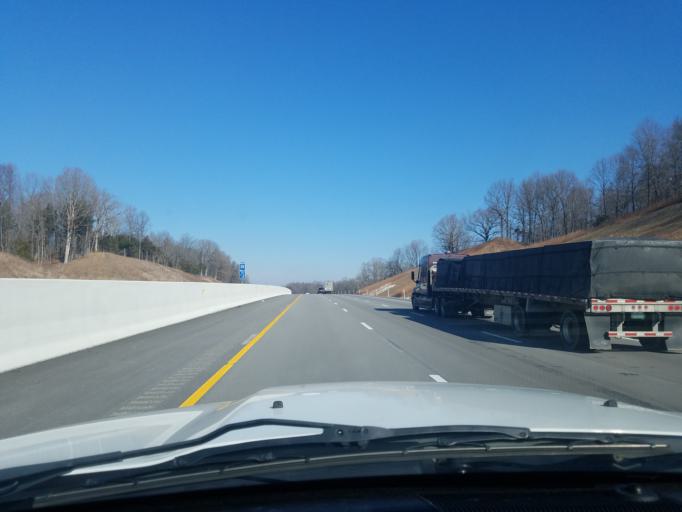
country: US
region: Kentucky
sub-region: Hart County
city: Munfordville
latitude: 37.3930
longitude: -85.8837
